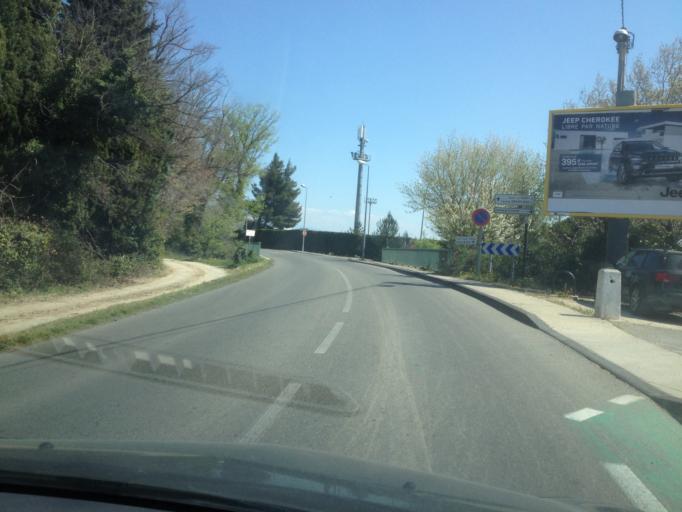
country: FR
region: Provence-Alpes-Cote d'Azur
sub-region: Departement du Vaucluse
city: Le Pontet
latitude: 43.9633
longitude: 4.8706
